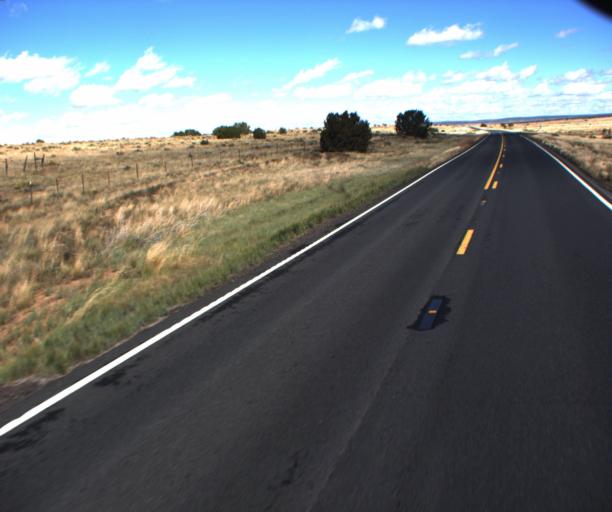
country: US
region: Arizona
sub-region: Apache County
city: Houck
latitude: 34.9623
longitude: -109.2281
